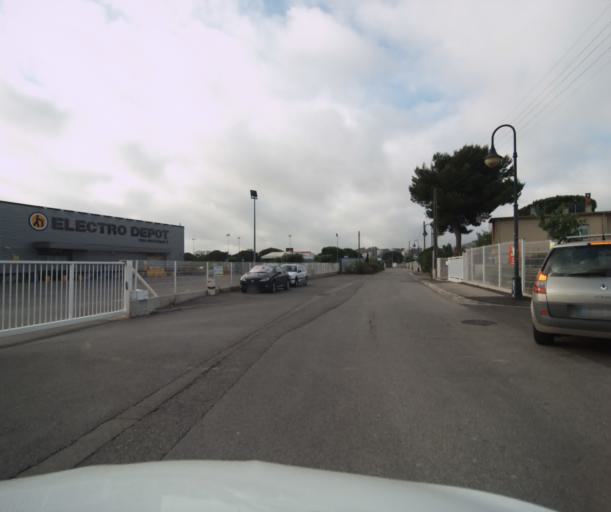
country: FR
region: Provence-Alpes-Cote d'Azur
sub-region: Departement du Var
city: Six-Fours-les-Plages
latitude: 43.1170
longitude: 5.8541
